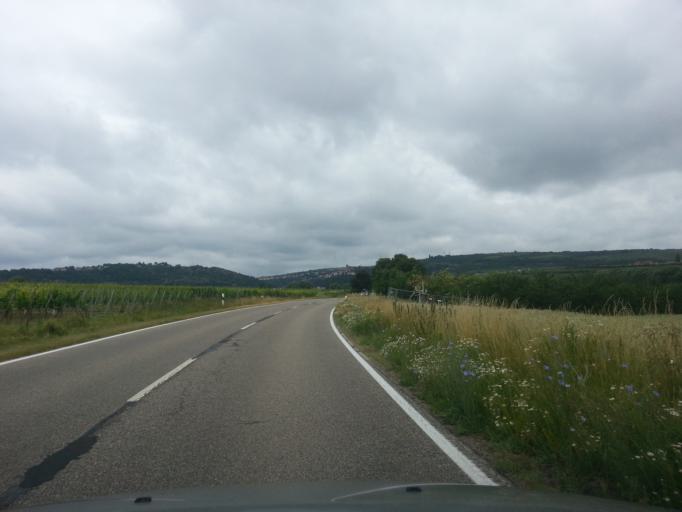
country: DE
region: Rheinland-Pfalz
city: Kirchheim an der Weinstrasse
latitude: 49.5385
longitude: 8.1711
